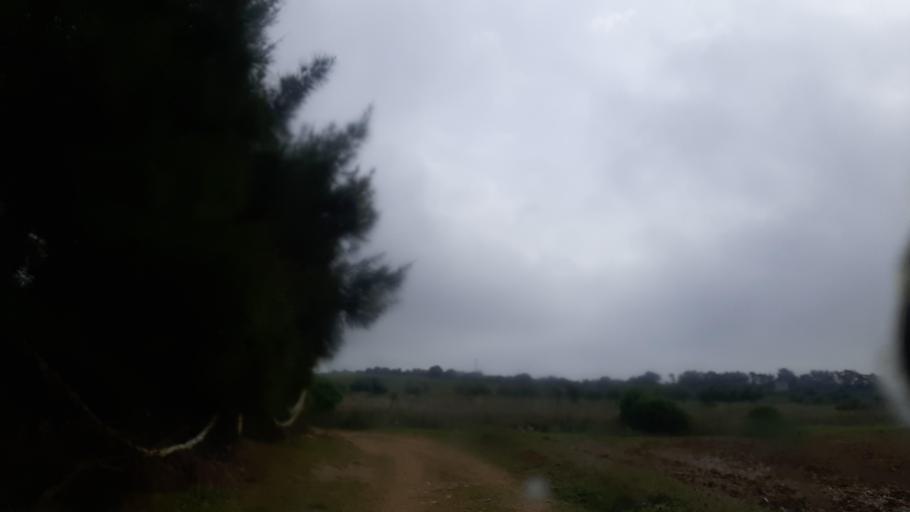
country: TN
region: Nabul
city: Qulaybiyah
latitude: 36.8254
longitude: 11.0366
